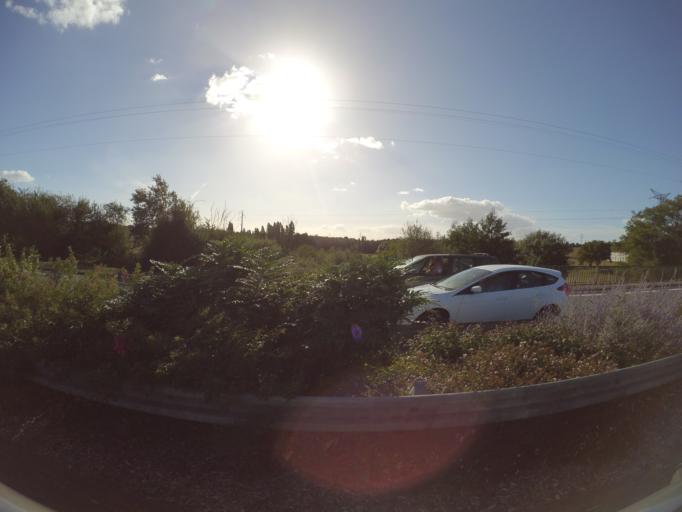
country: FR
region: Pays de la Loire
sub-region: Departement de Maine-et-Loire
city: Cholet
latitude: 47.0555
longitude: -0.9019
